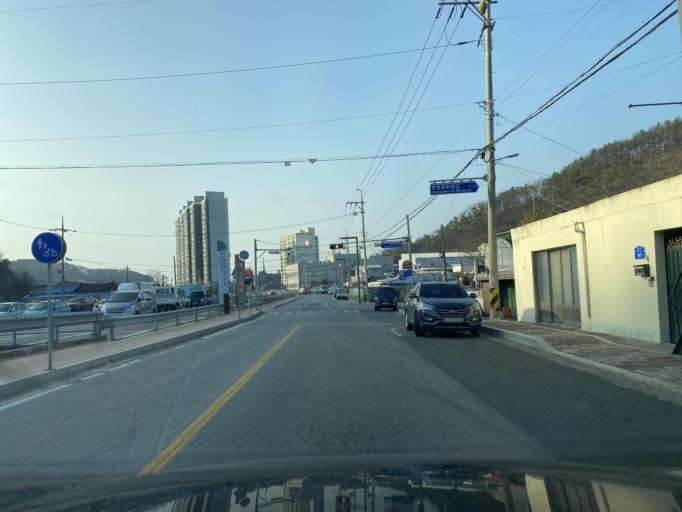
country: KR
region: Chungcheongnam-do
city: Yesan
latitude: 36.6773
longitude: 126.8409
